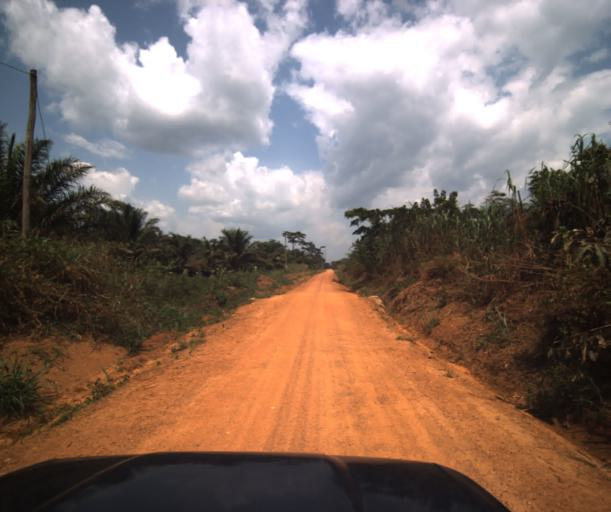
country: CM
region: Centre
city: Akono
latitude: 3.5581
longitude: 11.0737
